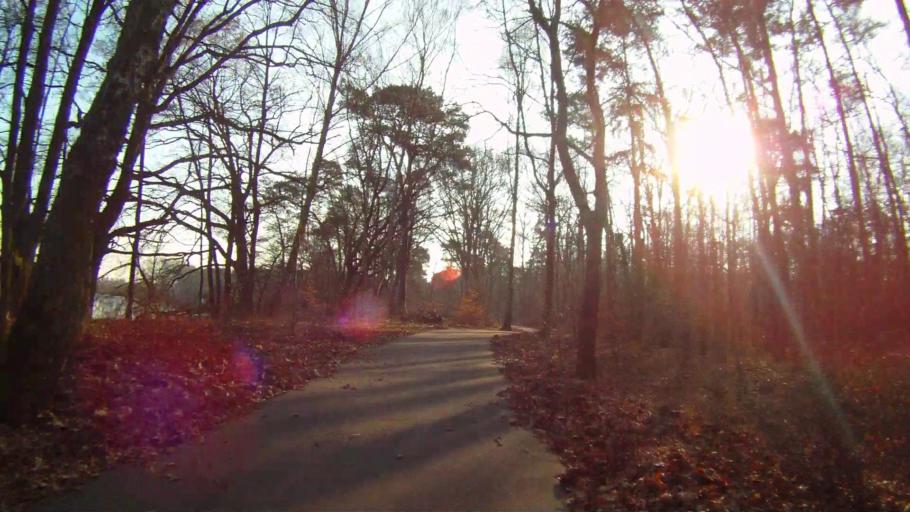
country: DE
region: Berlin
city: Rahnsdorf
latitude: 52.4287
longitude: 13.6738
